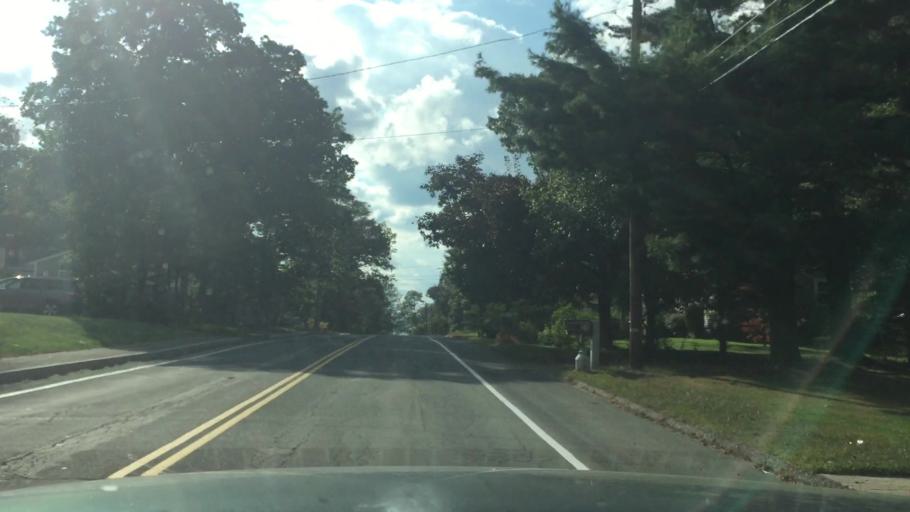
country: US
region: Massachusetts
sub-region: Norfolk County
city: Medway
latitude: 42.1572
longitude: -71.4138
